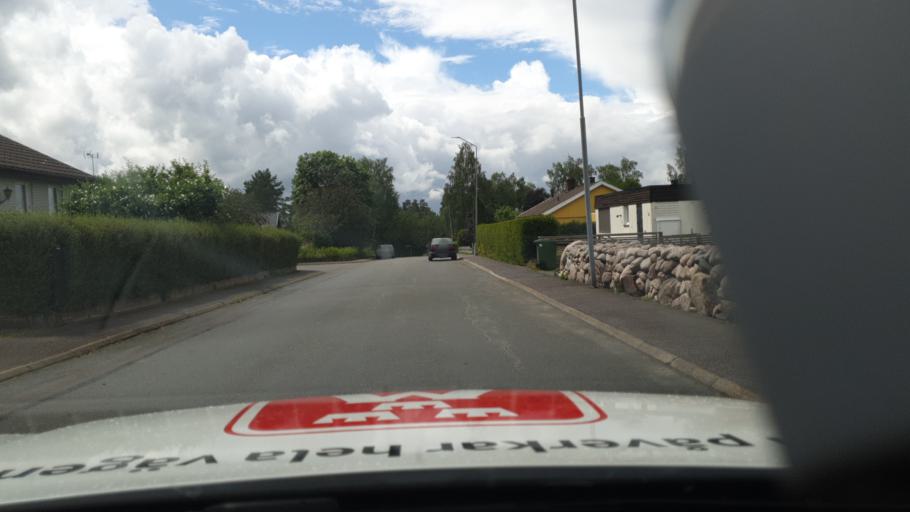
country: SE
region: Joenkoeping
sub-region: Mullsjo Kommun
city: Mullsjoe
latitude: 57.9185
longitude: 13.8692
